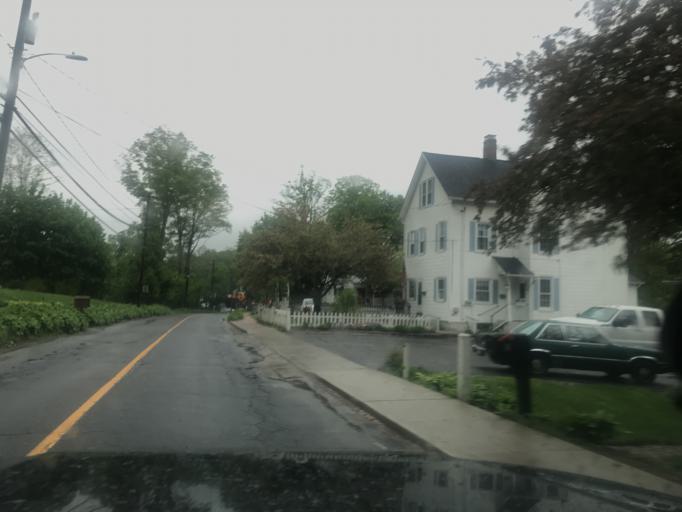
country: US
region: Connecticut
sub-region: Fairfield County
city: Bethel
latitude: 41.3697
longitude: -73.4067
